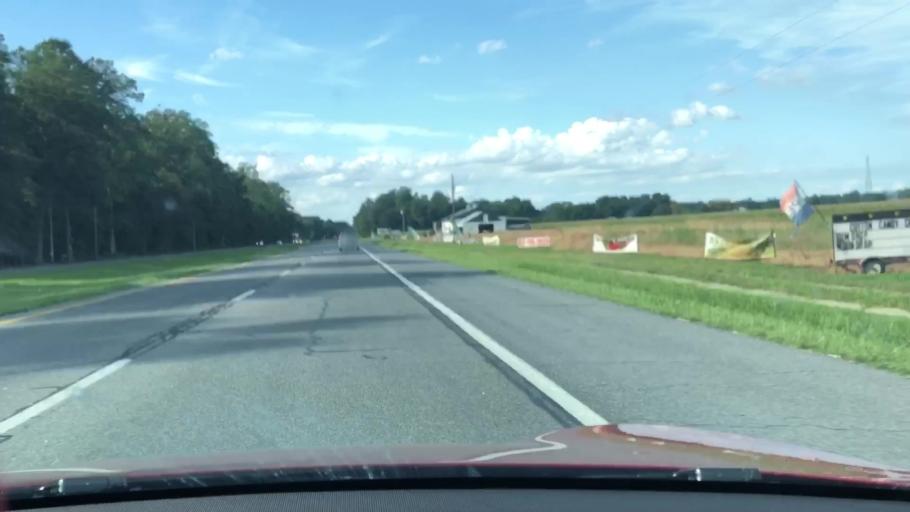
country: US
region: Delaware
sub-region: Kent County
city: Harrington
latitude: 38.9638
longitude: -75.5652
